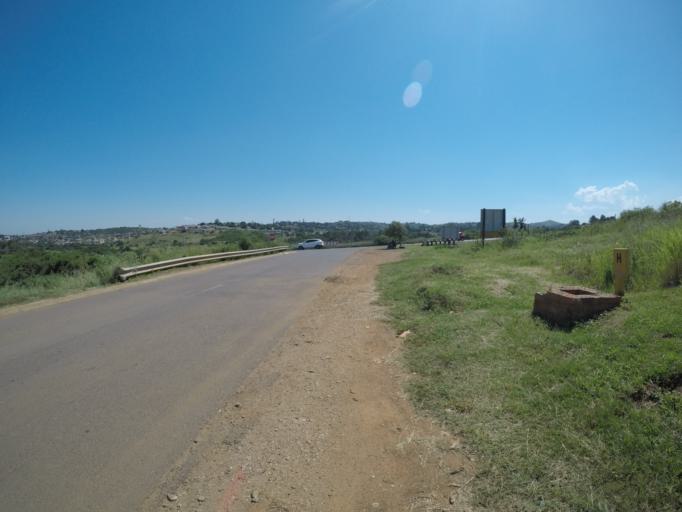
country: ZA
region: KwaZulu-Natal
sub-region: uThungulu District Municipality
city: Empangeni
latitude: -28.7650
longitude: 31.8765
